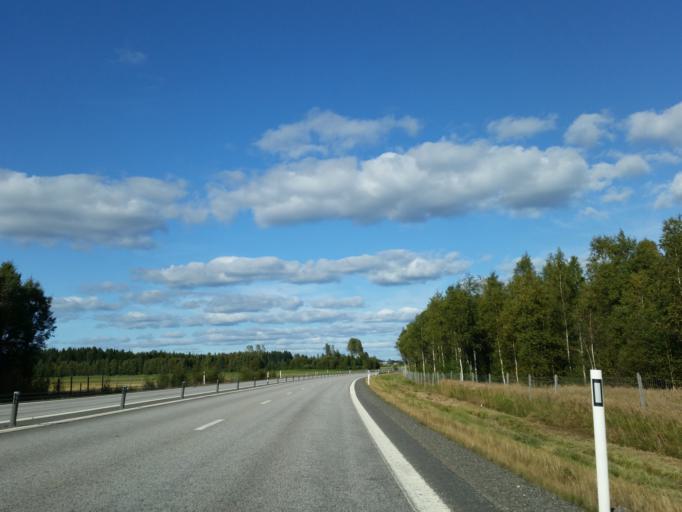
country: SE
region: Vaesterbotten
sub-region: Robertsfors Kommun
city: Robertsfors
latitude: 64.1427
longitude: 20.8968
